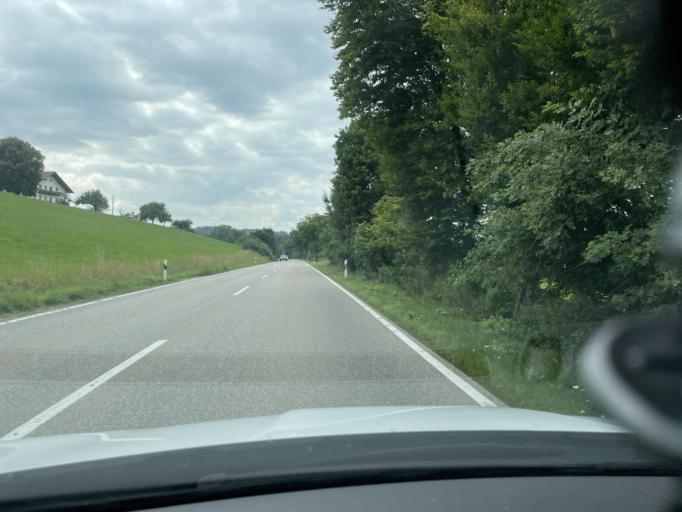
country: DE
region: Bavaria
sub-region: Upper Bavaria
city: Sankt Wolfgang
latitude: 48.2042
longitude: 12.1433
